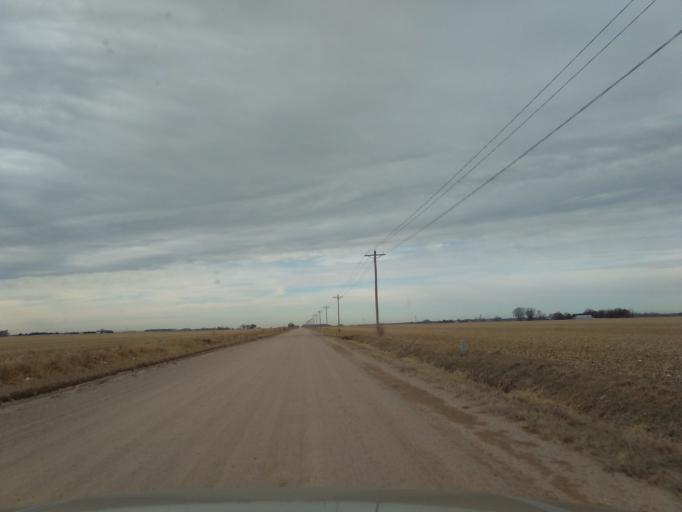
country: US
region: Nebraska
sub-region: Buffalo County
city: Gibbon
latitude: 40.6408
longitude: -98.9034
